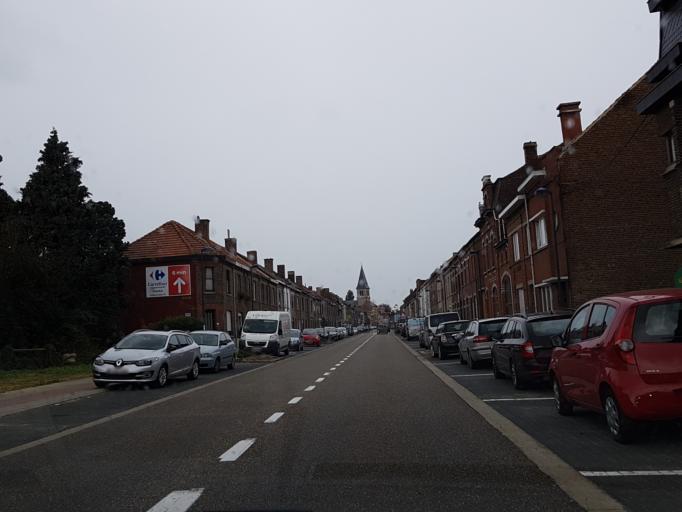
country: BE
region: Flanders
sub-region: Provincie Vlaams-Brabant
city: Tienen
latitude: 50.8005
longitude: 4.9589
